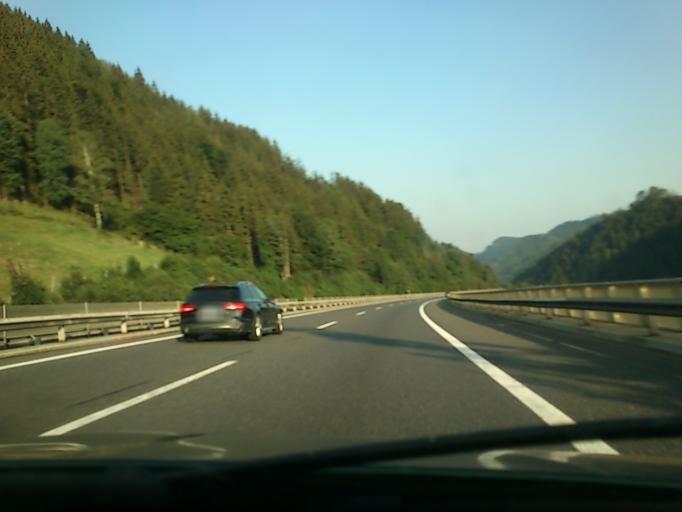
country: AT
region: Styria
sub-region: Politischer Bezirk Graz-Umgebung
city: Ubelbach
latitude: 47.2429
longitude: 15.1930
